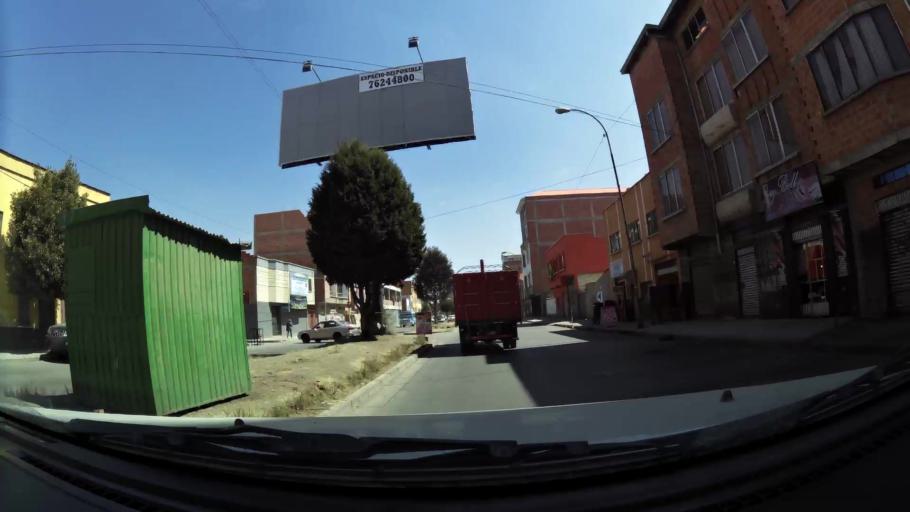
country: BO
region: La Paz
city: La Paz
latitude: -16.5249
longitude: -68.1486
